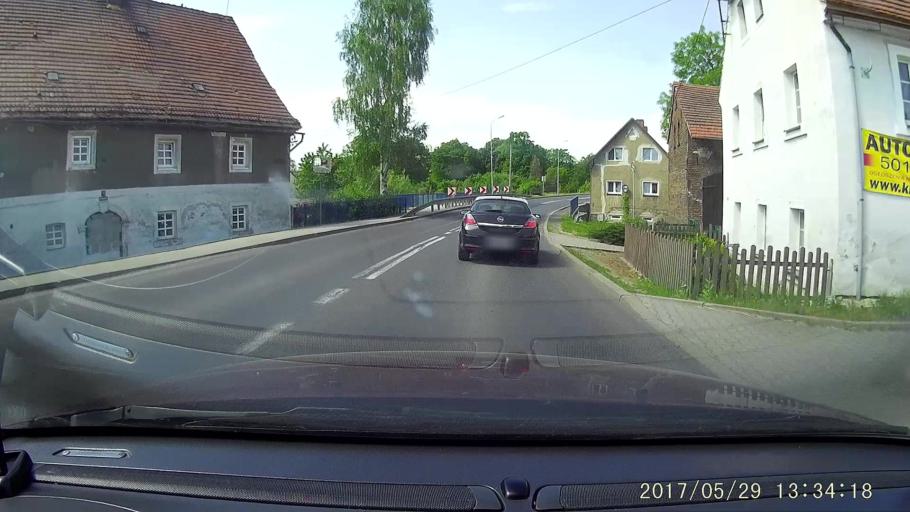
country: PL
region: Lower Silesian Voivodeship
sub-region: Powiat lubanski
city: Luban
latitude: 51.1029
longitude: 15.3048
